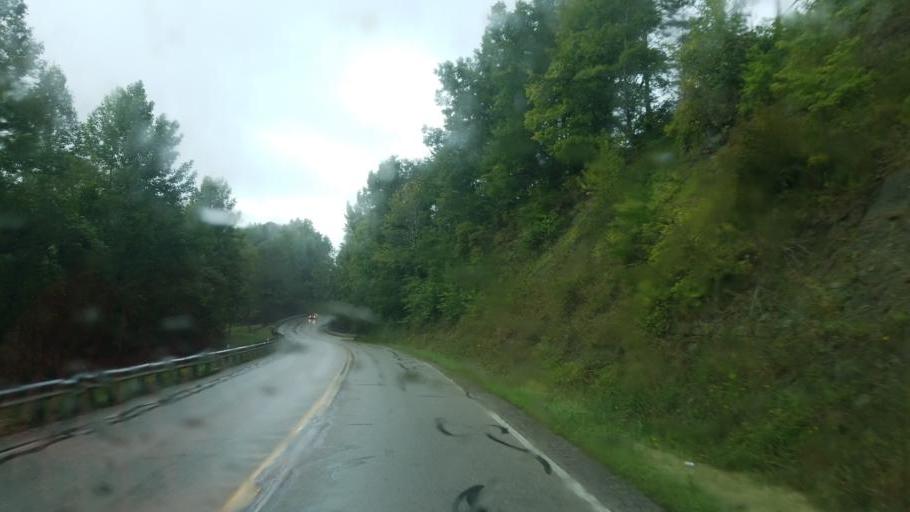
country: US
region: Kentucky
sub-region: Rowan County
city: Morehead
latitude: 38.1645
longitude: -83.4467
